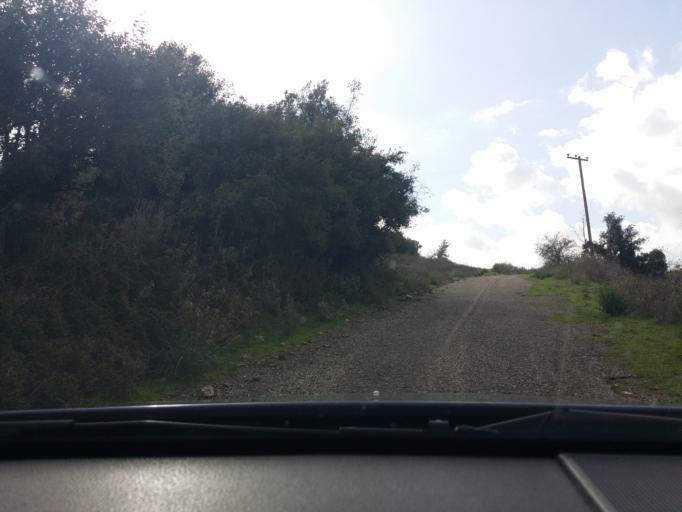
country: GR
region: West Greece
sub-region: Nomos Aitolias kai Akarnanias
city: Fitiai
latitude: 38.6676
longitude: 21.1905
